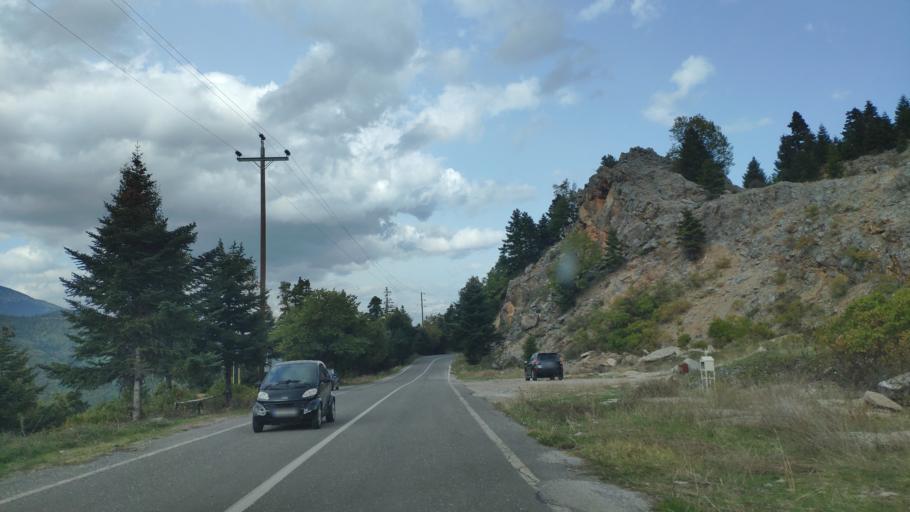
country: GR
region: Central Greece
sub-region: Nomos Fthiotidos
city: Anthili
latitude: 38.7349
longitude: 22.3692
